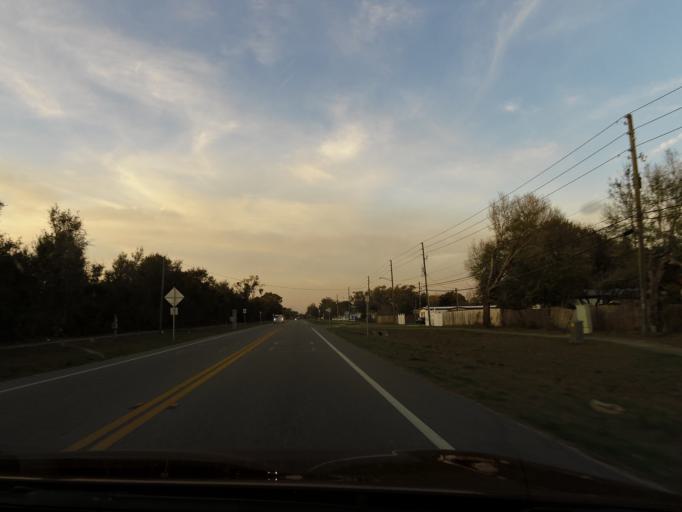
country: US
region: Florida
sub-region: Volusia County
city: North DeLand
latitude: 29.0734
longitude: -81.3048
